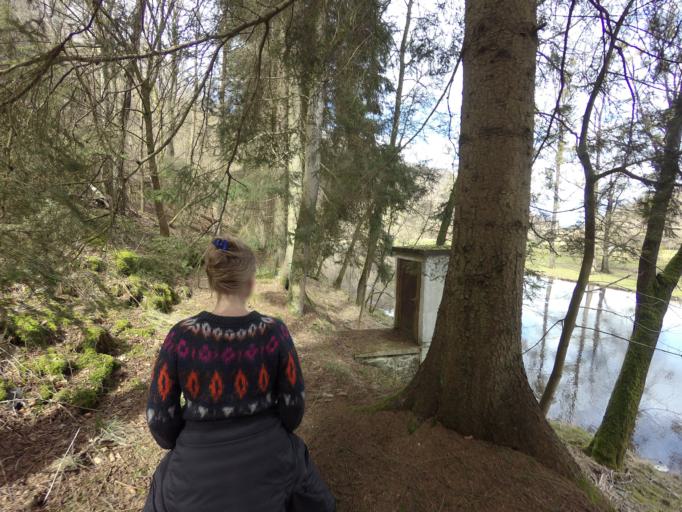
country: BE
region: Wallonia
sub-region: Province de Liege
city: Aywaille
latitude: 50.4265
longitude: 5.7313
